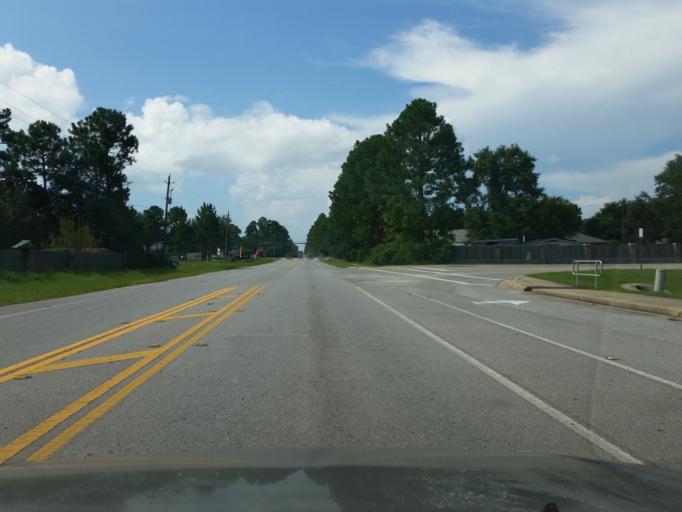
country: US
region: Florida
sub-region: Escambia County
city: Myrtle Grove
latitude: 30.3438
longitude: -87.4032
